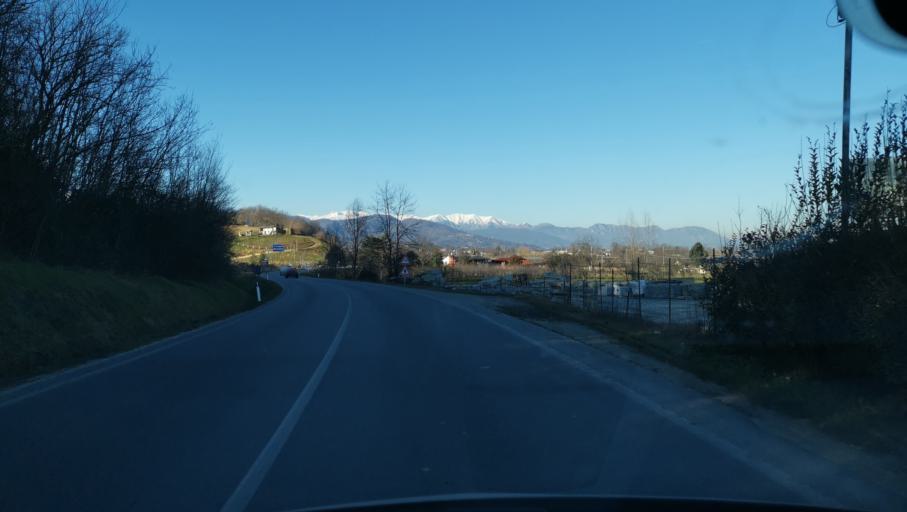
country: IT
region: Piedmont
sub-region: Provincia di Torino
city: Bibiana
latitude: 44.7797
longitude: 7.3005
